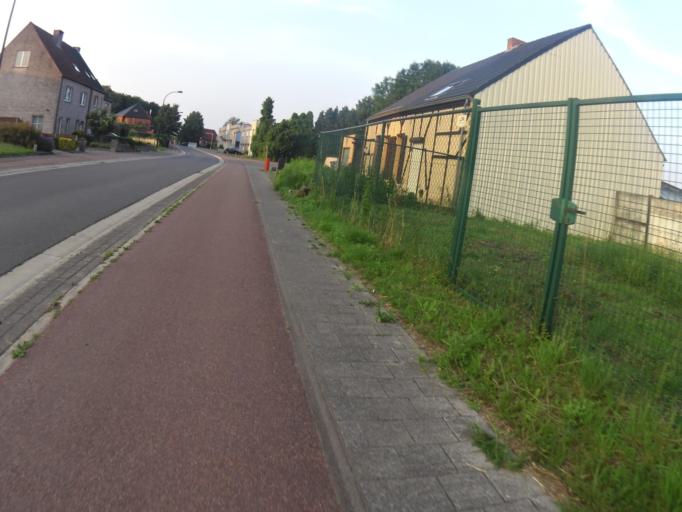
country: BE
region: Flanders
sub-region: Provincie Antwerpen
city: Geel
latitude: 51.1627
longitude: 5.0191
